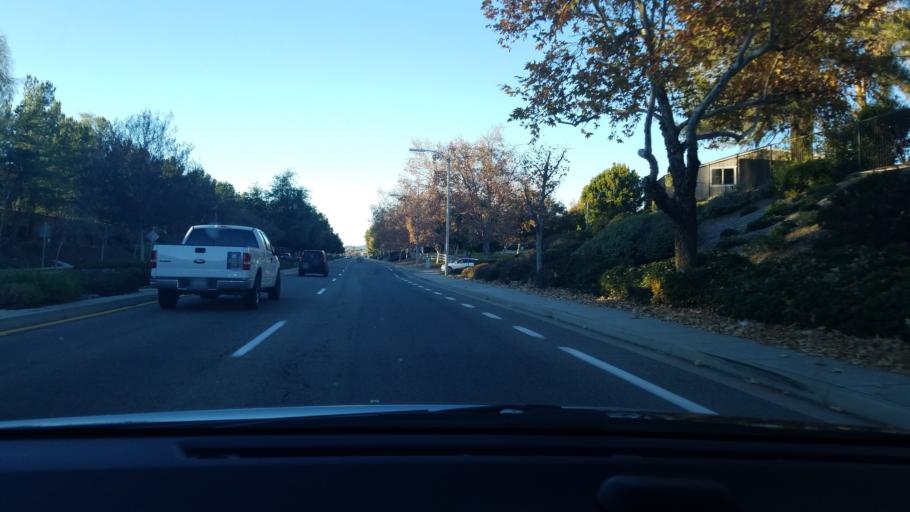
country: US
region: California
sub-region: Riverside County
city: Murrieta Hot Springs
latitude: 33.5424
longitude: -117.1514
